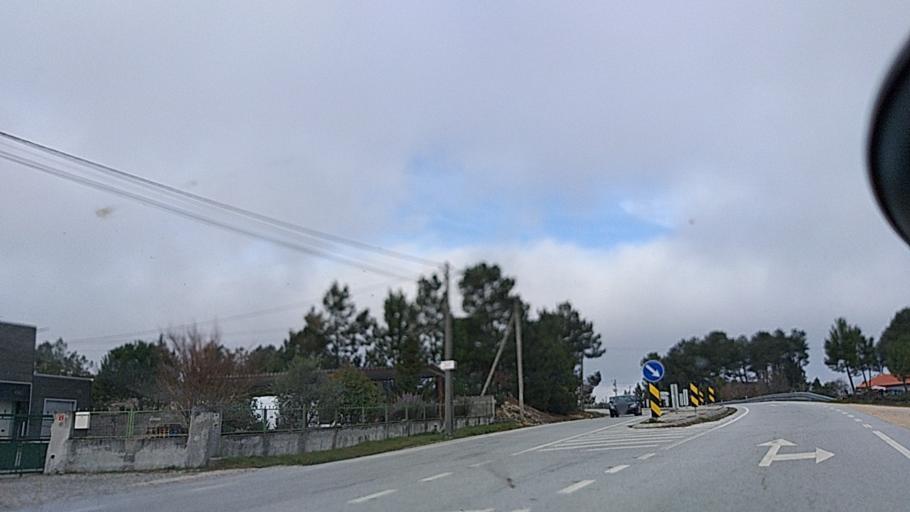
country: PT
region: Guarda
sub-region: Aguiar da Beira
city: Aguiar da Beira
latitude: 40.7882
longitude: -7.5037
